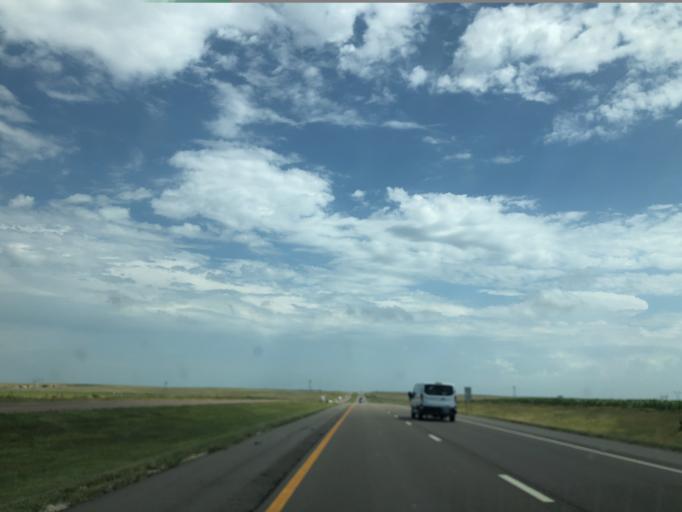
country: US
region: Kansas
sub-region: Logan County
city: Oakley
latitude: 39.2715
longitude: -100.9366
